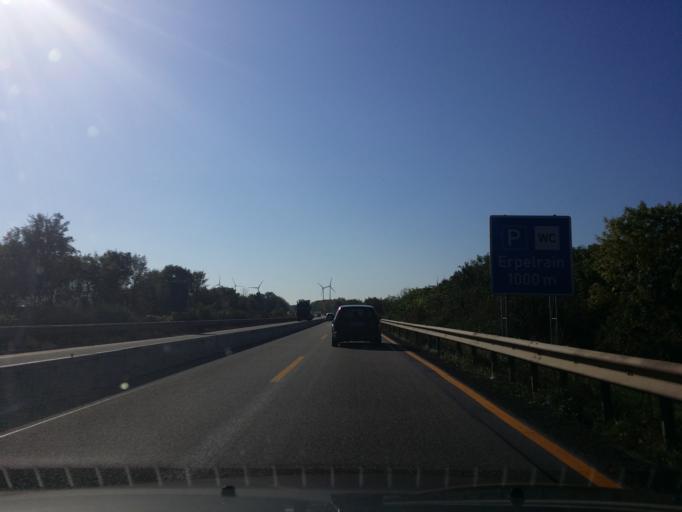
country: DE
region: Rheinland-Pfalz
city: Kleinniedesheim
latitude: 49.6075
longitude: 8.2891
